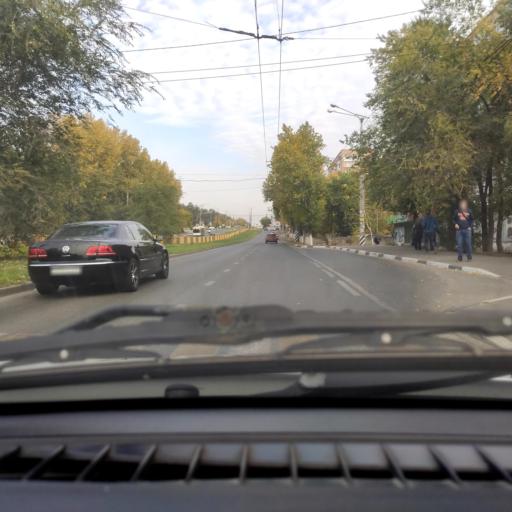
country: RU
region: Samara
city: Zhigulevsk
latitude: 53.4840
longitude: 49.4743
